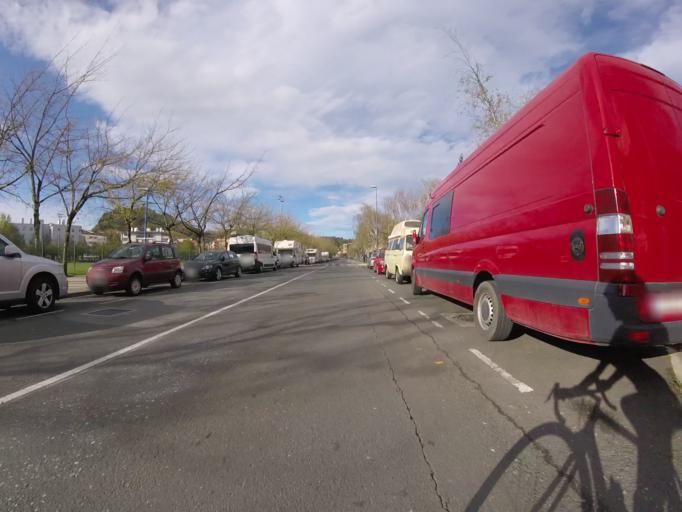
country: ES
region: Basque Country
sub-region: Provincia de Guipuzcoa
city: Hernani
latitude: 43.2720
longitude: -1.9727
